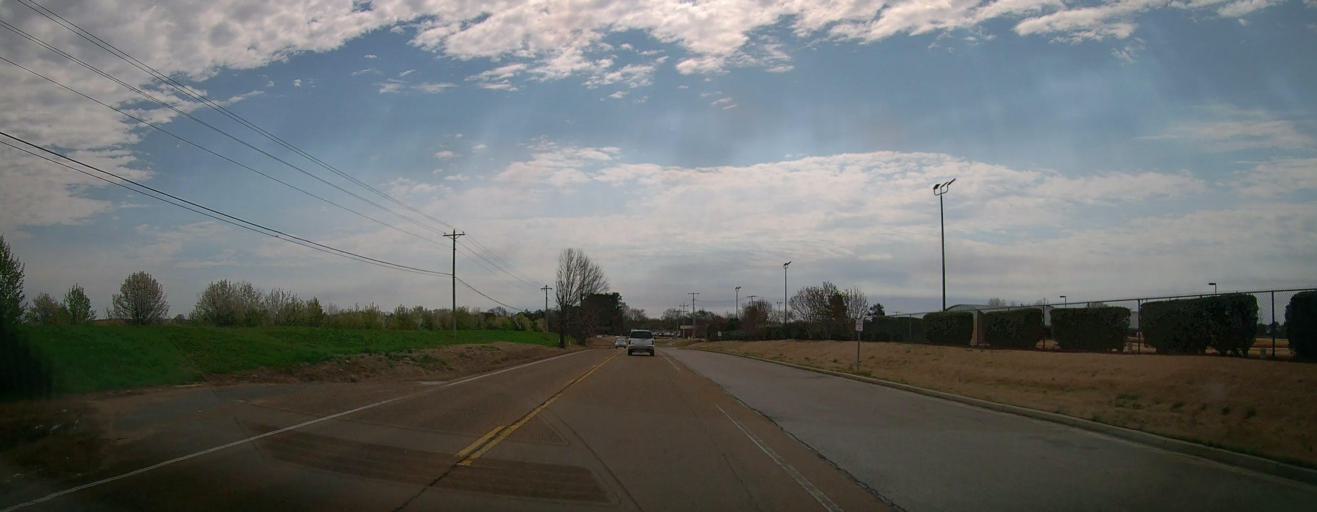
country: US
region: Mississippi
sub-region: De Soto County
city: Olive Branch
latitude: 34.9288
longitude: -89.7900
